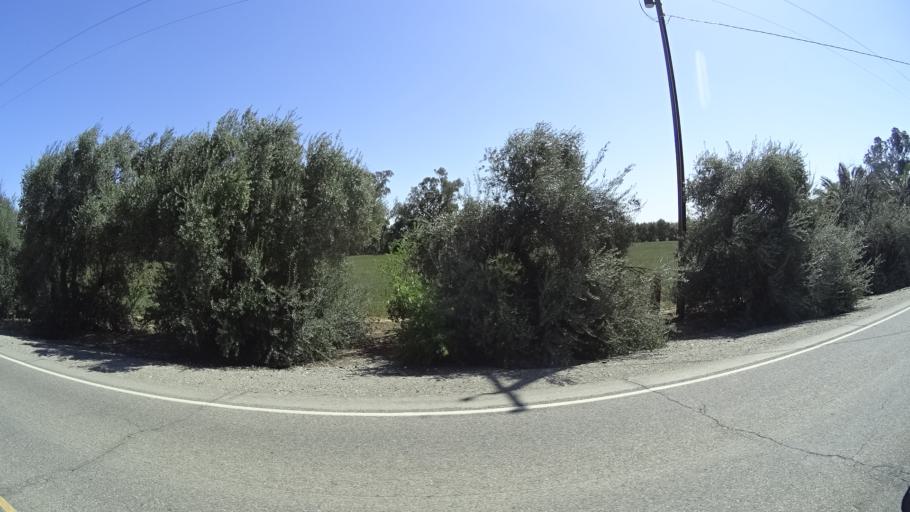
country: US
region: California
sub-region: Glenn County
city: Orland
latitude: 39.7092
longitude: -122.1971
